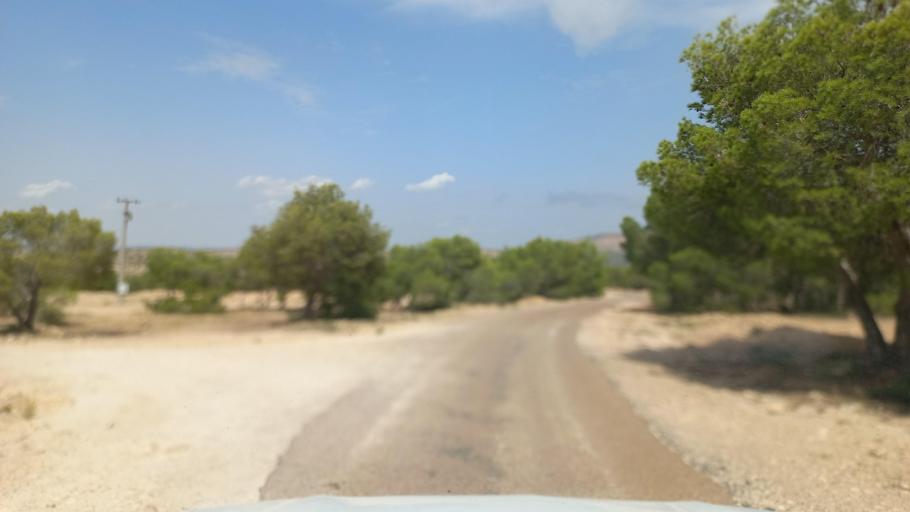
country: TN
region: Al Qasrayn
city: Sbiba
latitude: 35.3941
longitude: 8.9108
